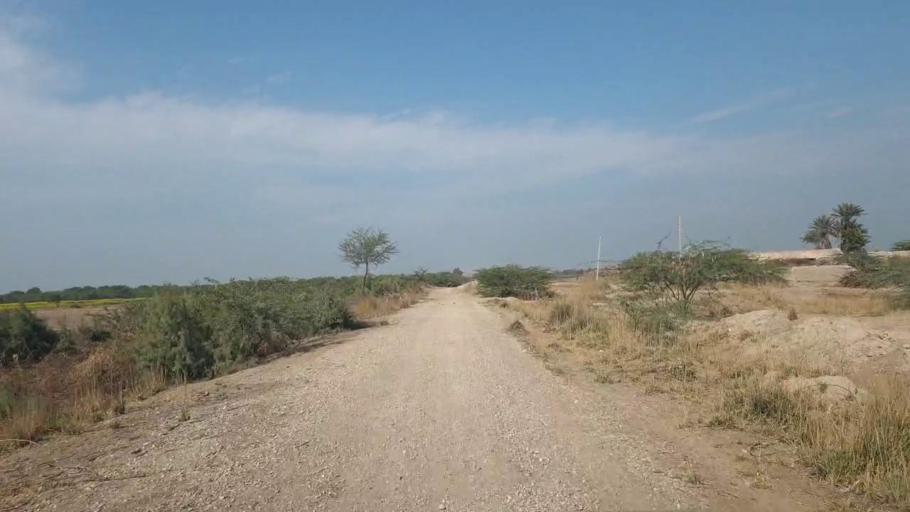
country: PK
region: Sindh
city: Shahdadpur
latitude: 25.9906
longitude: 68.5475
